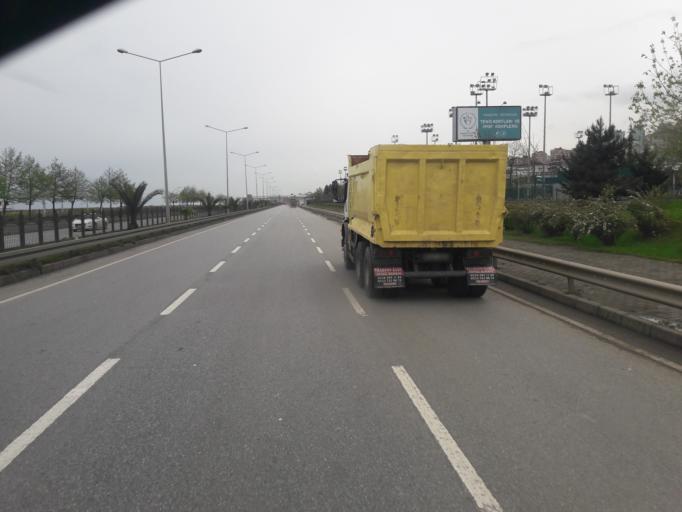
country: TR
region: Trabzon
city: Trabzon
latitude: 40.9967
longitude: 39.6689
